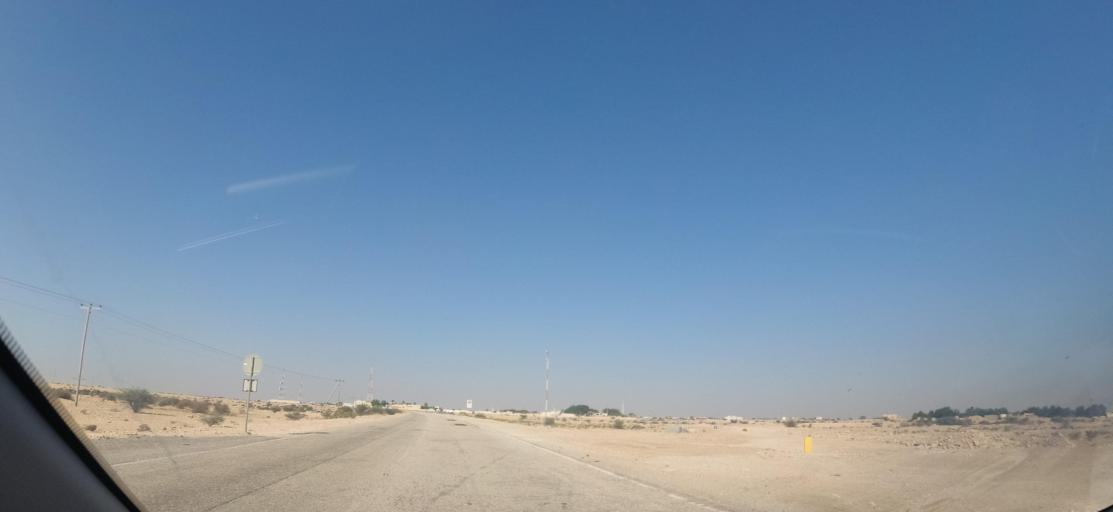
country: QA
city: Al Jumayliyah
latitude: 25.6109
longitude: 51.0780
